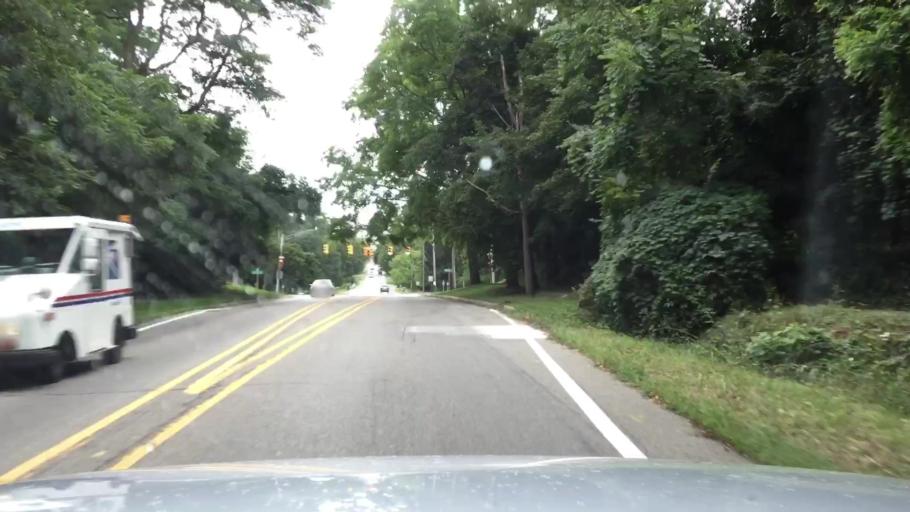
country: US
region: Michigan
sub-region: Oakland County
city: Birmingham
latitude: 42.5769
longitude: -83.2073
